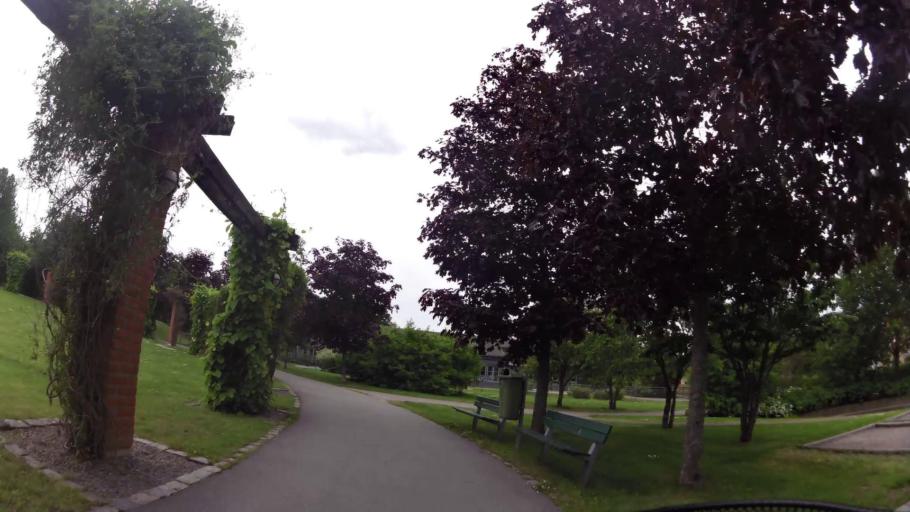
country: SE
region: OEstergoetland
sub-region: Linkopings Kommun
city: Malmslatt
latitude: 58.3861
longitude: 15.5592
